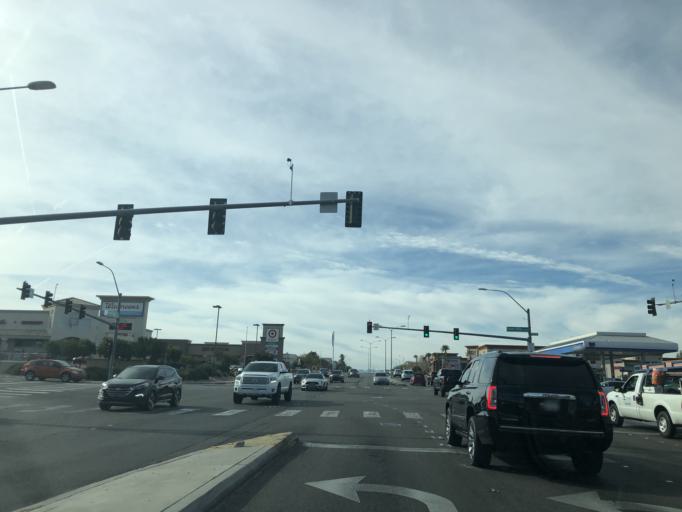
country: US
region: Nevada
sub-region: Clark County
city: Whitney
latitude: 36.0058
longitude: -115.0827
